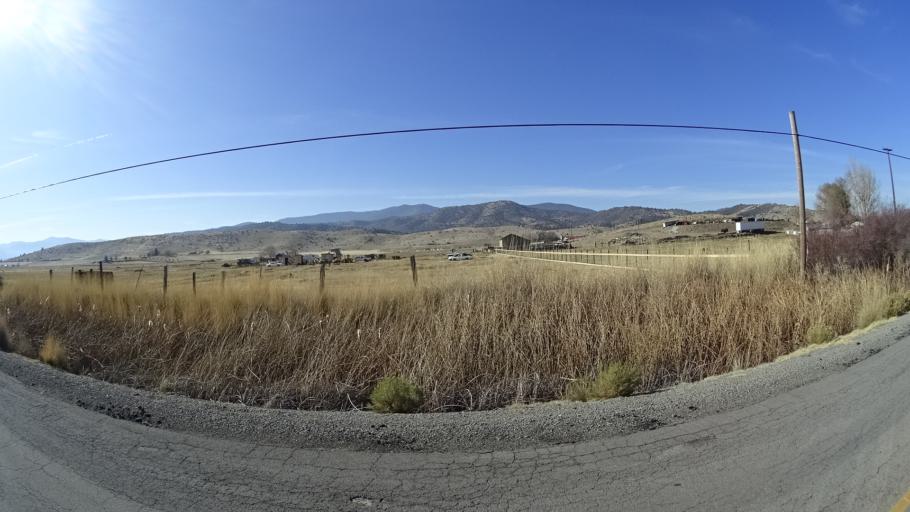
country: US
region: California
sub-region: Siskiyou County
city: Montague
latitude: 41.6123
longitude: -122.5230
